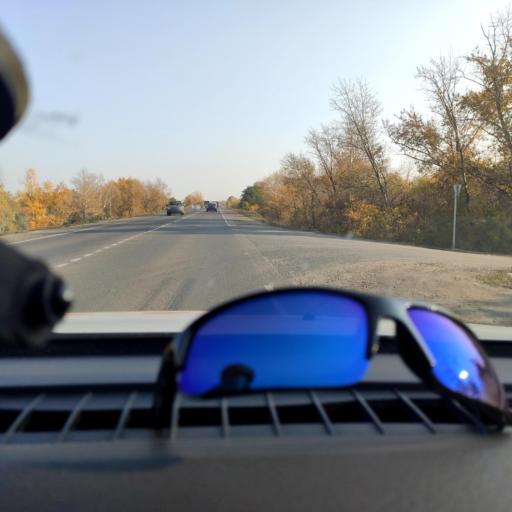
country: RU
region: Samara
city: Samara
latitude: 53.1056
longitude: 50.1360
